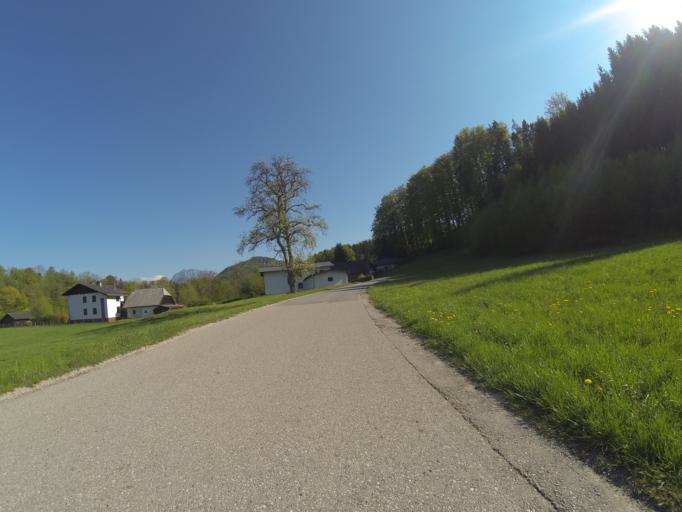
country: AT
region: Upper Austria
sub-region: Politischer Bezirk Gmunden
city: Altmunster
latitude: 47.9401
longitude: 13.7516
